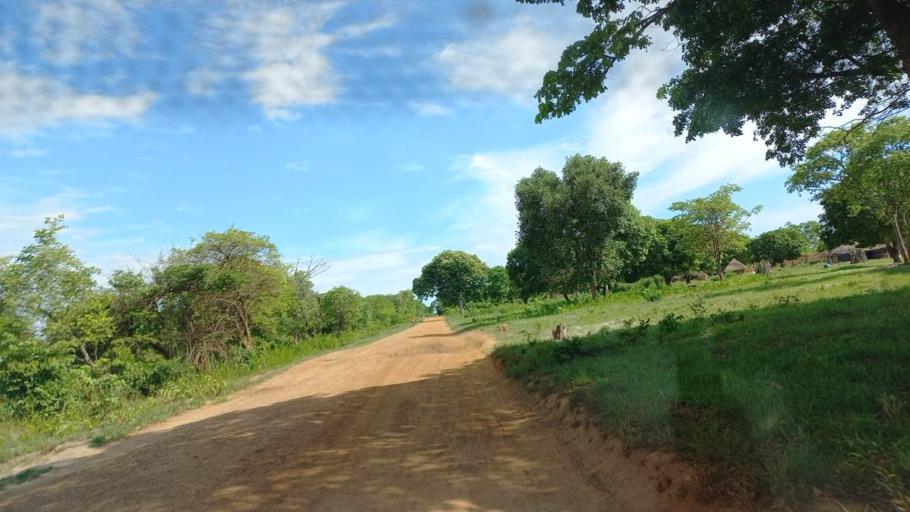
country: ZM
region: North-Western
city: Kabompo
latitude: -13.0675
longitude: 24.2185
